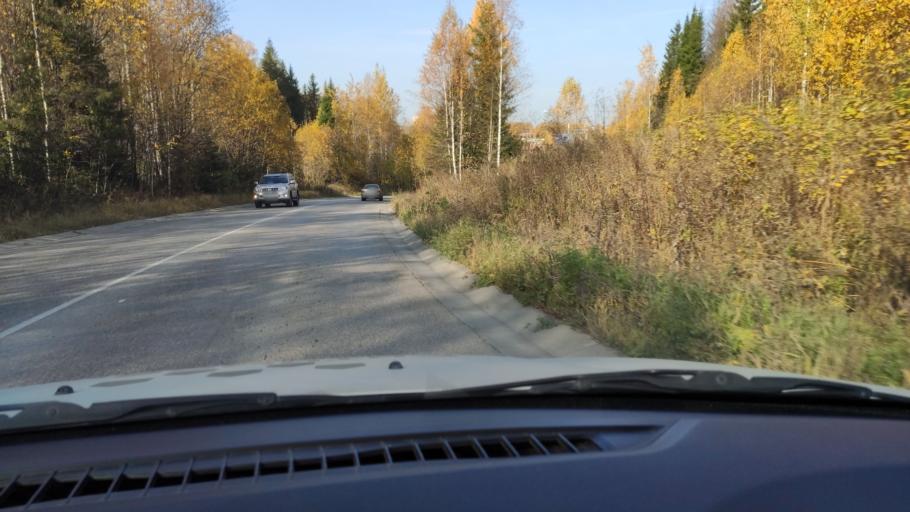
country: RU
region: Perm
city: Novyye Lyady
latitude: 58.0402
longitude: 56.5992
